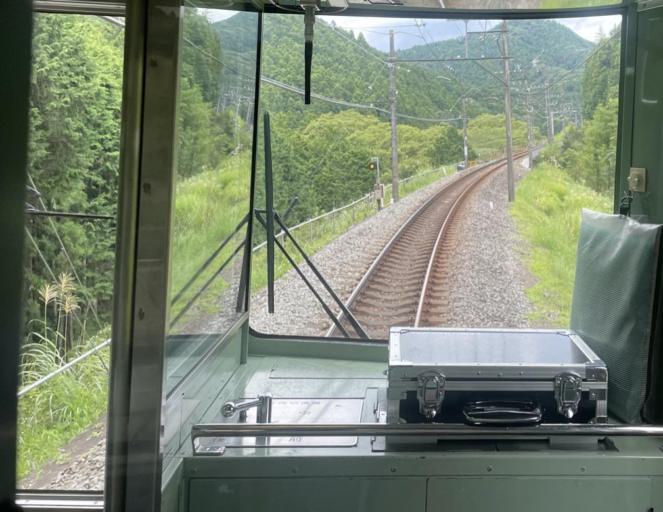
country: JP
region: Saitama
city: Morohongo
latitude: 35.9192
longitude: 139.2070
